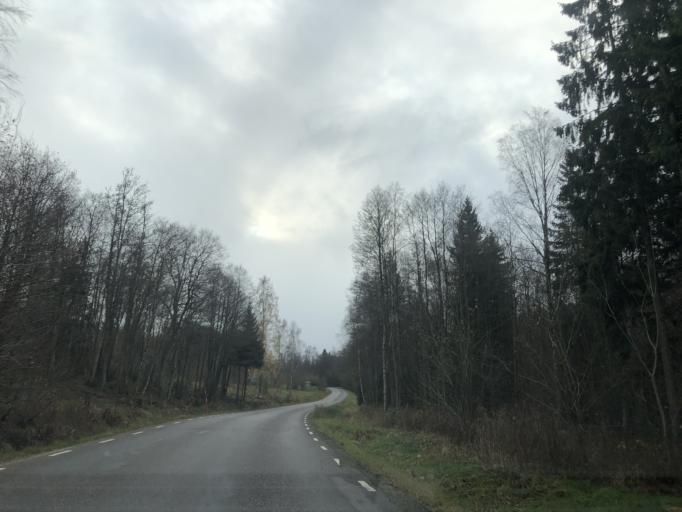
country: SE
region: Vaestra Goetaland
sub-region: Ulricehamns Kommun
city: Ulricehamn
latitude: 57.6779
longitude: 13.4088
